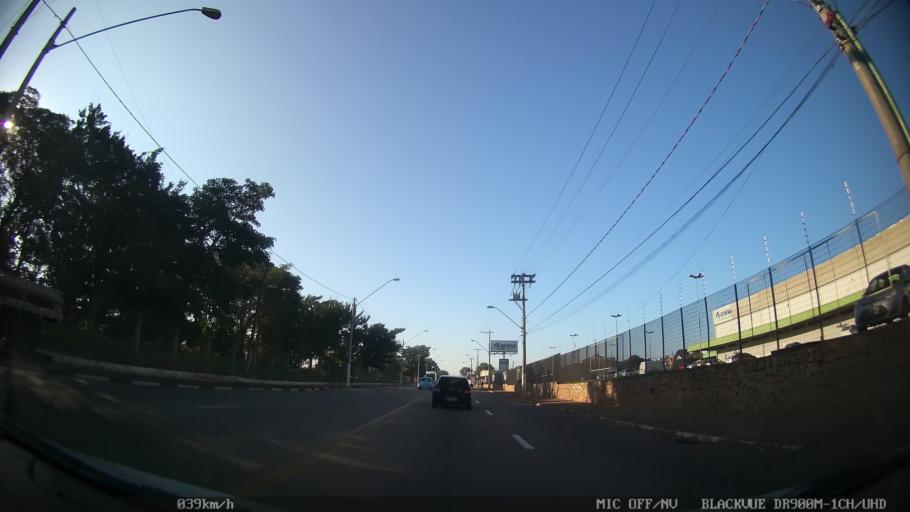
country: BR
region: Sao Paulo
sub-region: Sumare
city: Sumare
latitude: -22.8122
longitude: -47.2760
